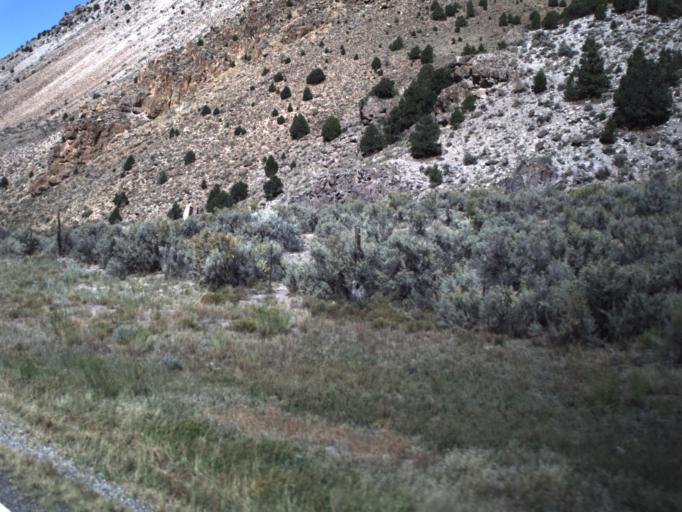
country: US
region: Utah
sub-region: Piute County
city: Junction
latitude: 38.1830
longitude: -112.0818
